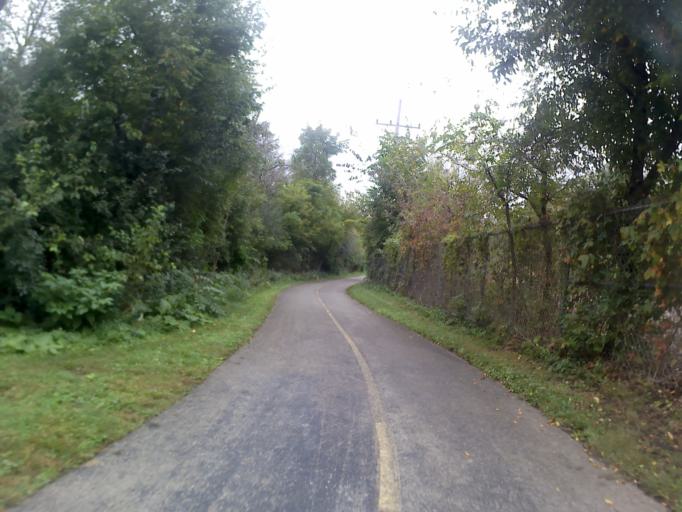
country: US
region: Illinois
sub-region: Kendall County
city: Oswego
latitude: 41.6946
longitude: -88.3476
